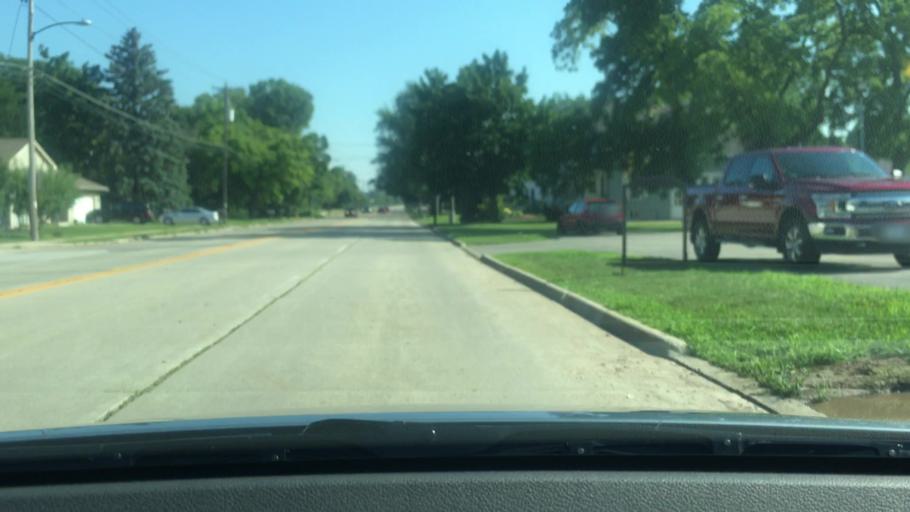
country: US
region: Wisconsin
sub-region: Winnebago County
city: Oshkosh
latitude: 43.9914
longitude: -88.5426
